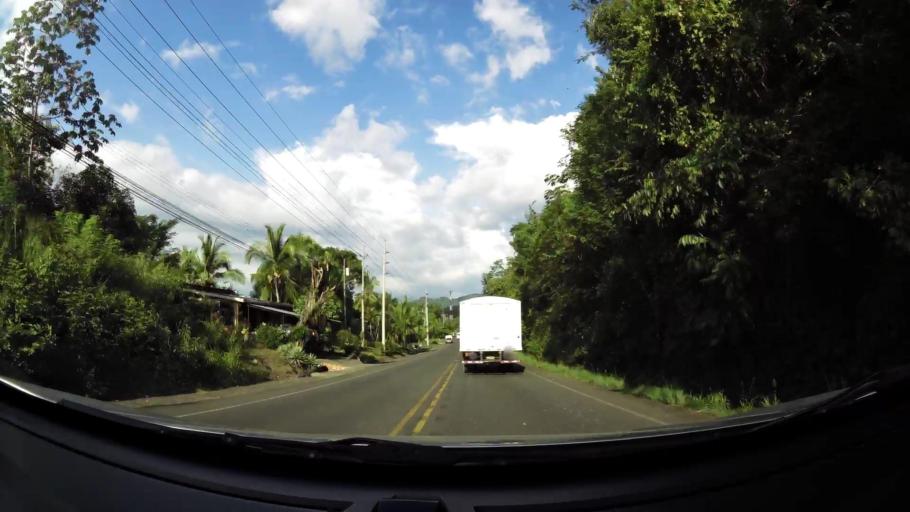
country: CR
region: Puntarenas
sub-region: Canton de Garabito
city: Jaco
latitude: 9.7513
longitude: -84.6285
